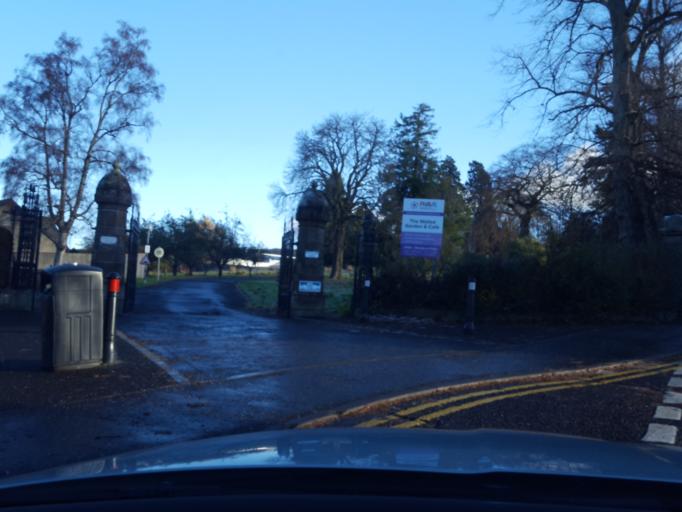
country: GB
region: Scotland
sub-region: Perth and Kinross
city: Perth
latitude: 56.4005
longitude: -3.4200
